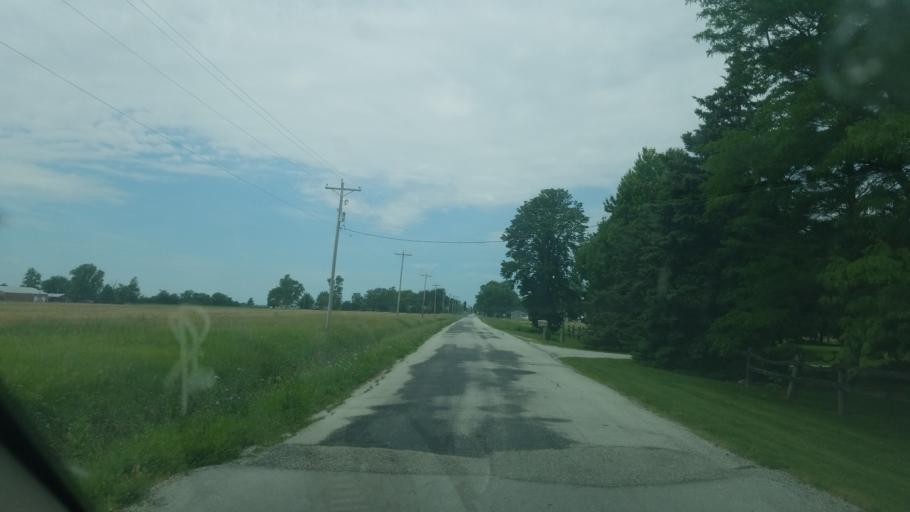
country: US
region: Ohio
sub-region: Wood County
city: North Baltimore
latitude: 41.2686
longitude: -83.6645
